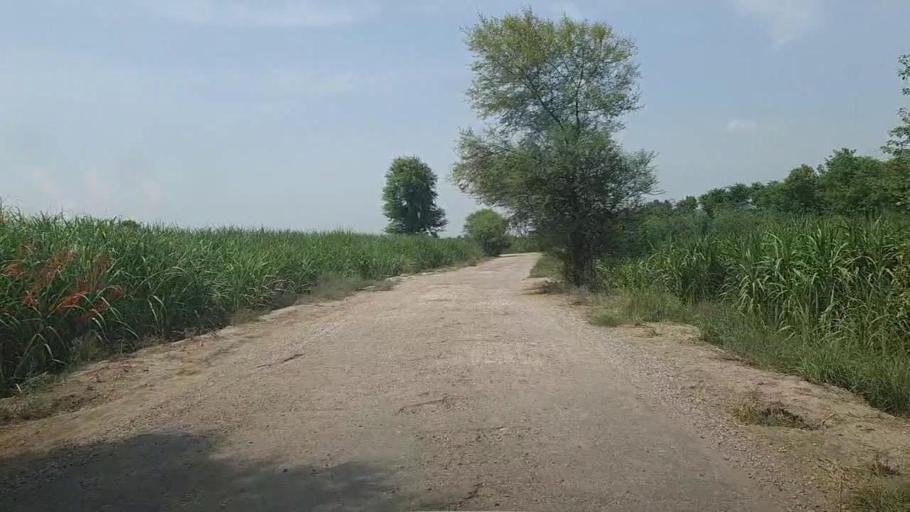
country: PK
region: Sindh
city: Ubauro
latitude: 28.1677
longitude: 69.8316
